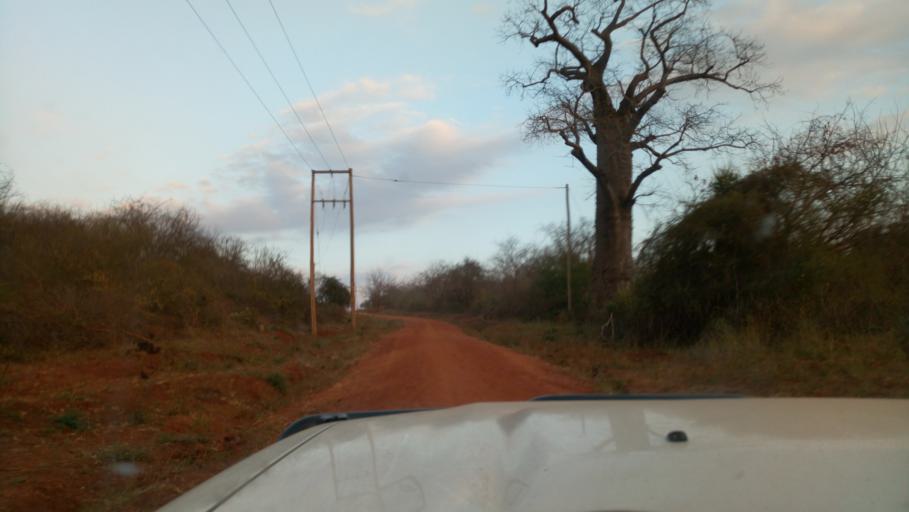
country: KE
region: Kitui
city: Kitui
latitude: -1.6991
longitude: 38.2387
